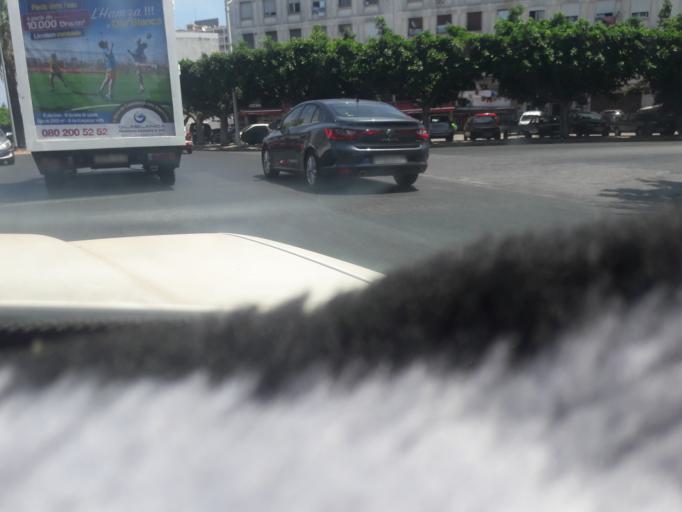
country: MA
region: Grand Casablanca
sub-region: Casablanca
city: Casablanca
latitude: 33.5841
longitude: -7.6505
